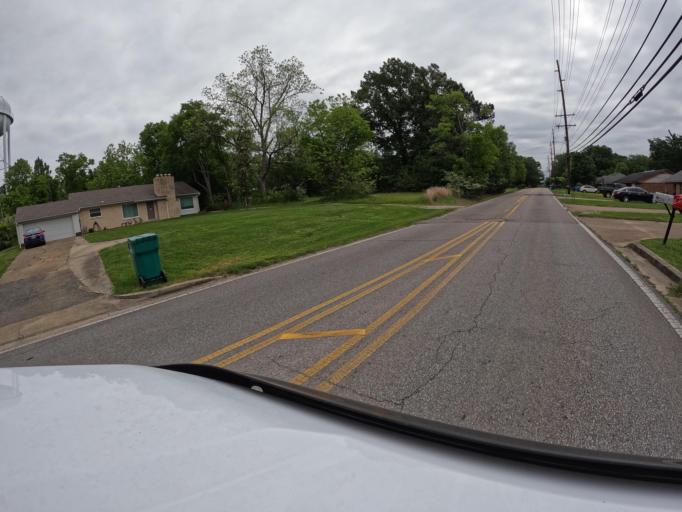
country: US
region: Mississippi
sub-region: Lee County
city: Tupelo
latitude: 34.2647
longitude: -88.7457
